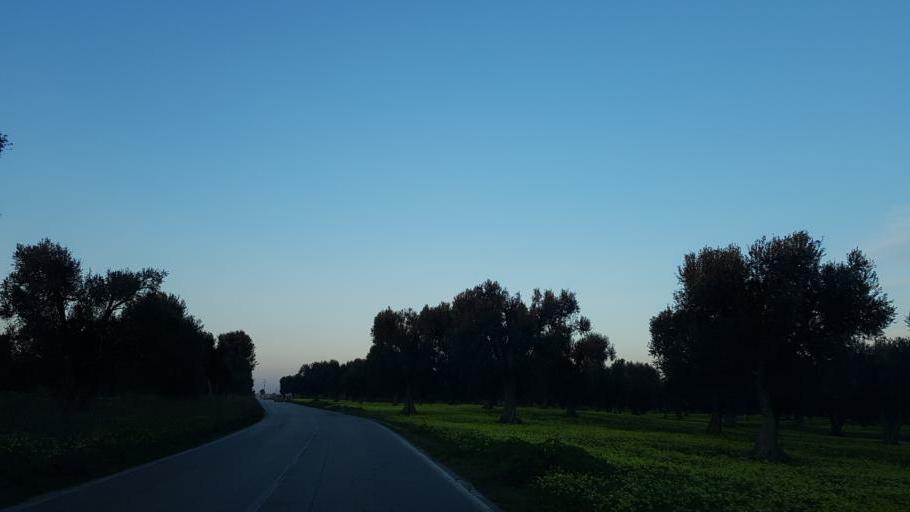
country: IT
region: Apulia
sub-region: Provincia di Brindisi
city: Tuturano
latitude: 40.5638
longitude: 17.9489
